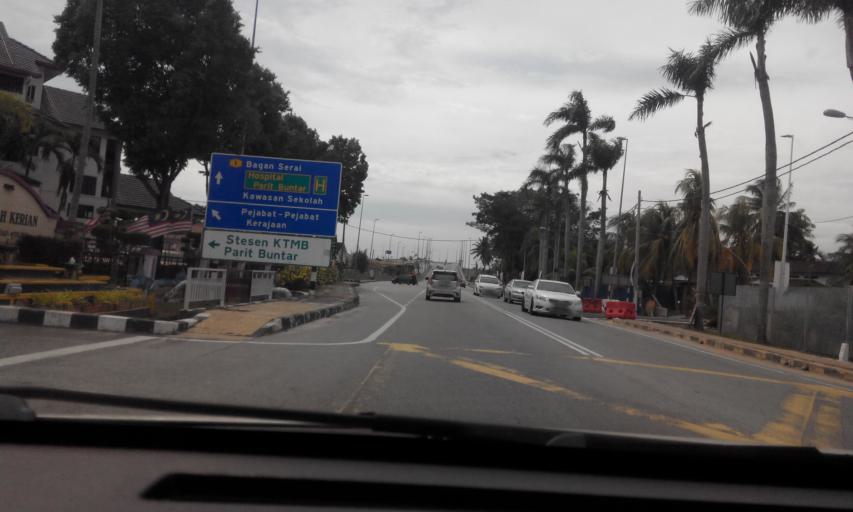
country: MY
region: Perak
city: Parit Buntar
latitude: 5.1300
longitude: 100.4900
